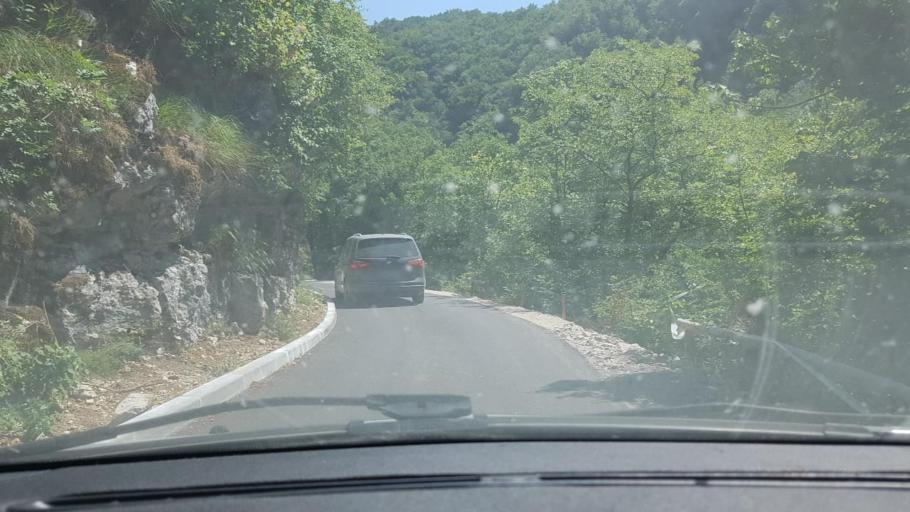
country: BA
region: Federation of Bosnia and Herzegovina
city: Orasac
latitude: 44.6260
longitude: 16.0471
